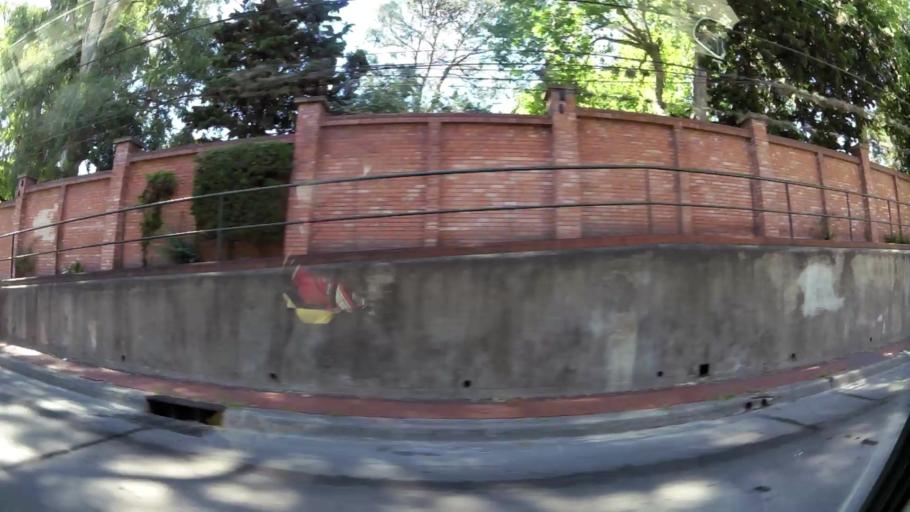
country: AR
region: Buenos Aires
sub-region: Partido de Vicente Lopez
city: Olivos
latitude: -34.5124
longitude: -58.4808
